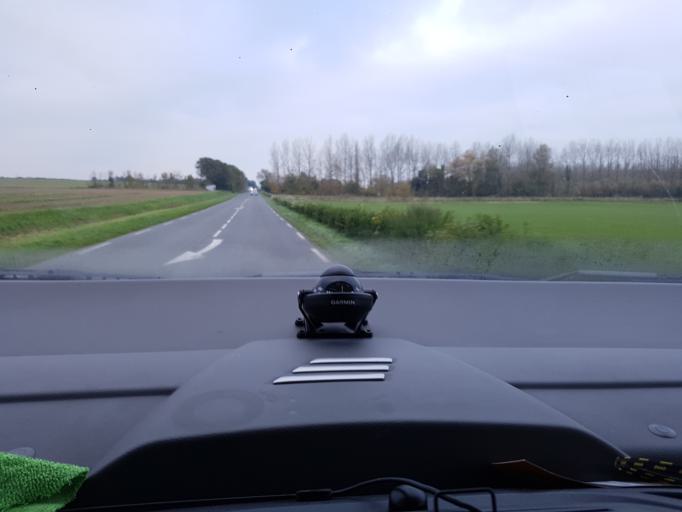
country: FR
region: Picardie
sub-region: Departement de la Somme
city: Bethencourt-sur-Mer
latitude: 50.1297
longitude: 1.4995
